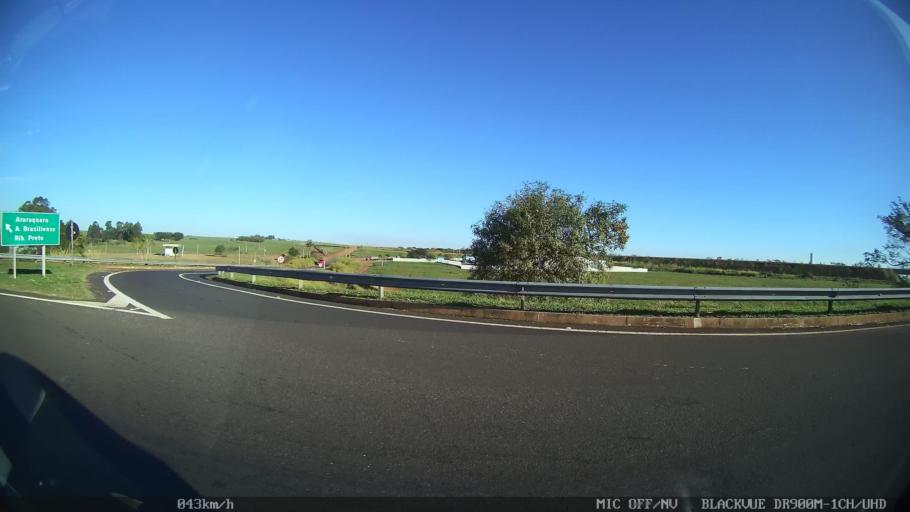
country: BR
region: Sao Paulo
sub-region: Americo Brasiliense
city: Americo Brasiliense
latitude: -21.7758
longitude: -48.1006
